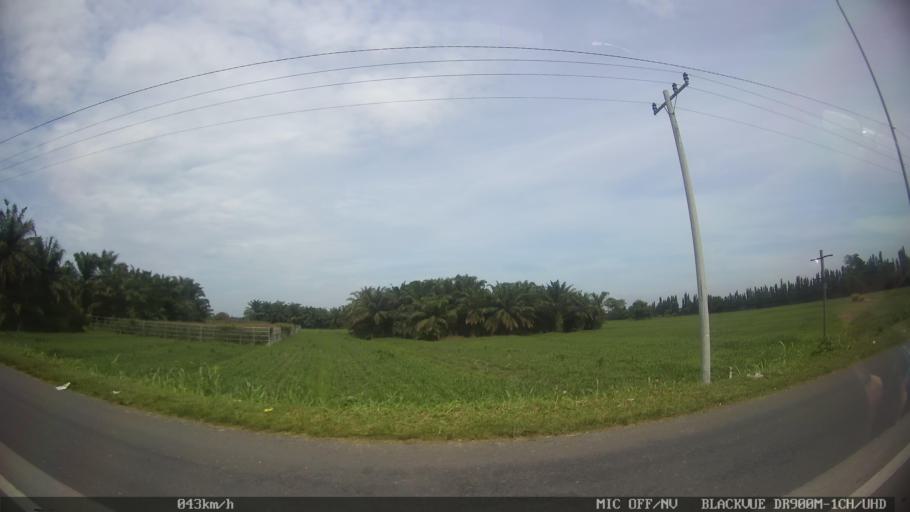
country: ID
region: North Sumatra
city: Sunggal
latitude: 3.6236
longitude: 98.6279
